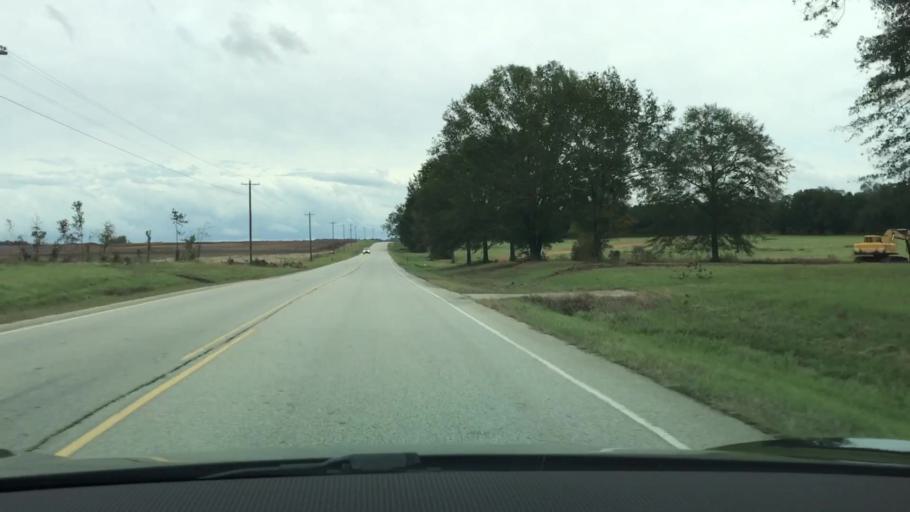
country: US
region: Georgia
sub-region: Jefferson County
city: Wrens
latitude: 33.1161
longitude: -82.4369
